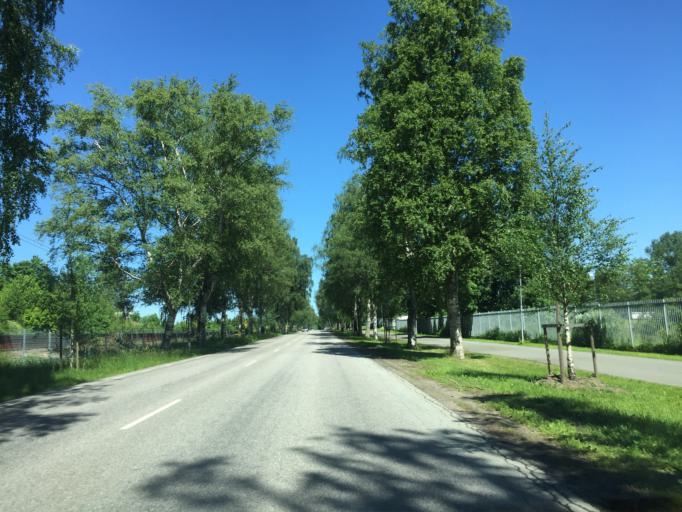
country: SE
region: OErebro
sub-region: Orebro Kommun
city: Orebro
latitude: 59.2580
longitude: 15.1885
